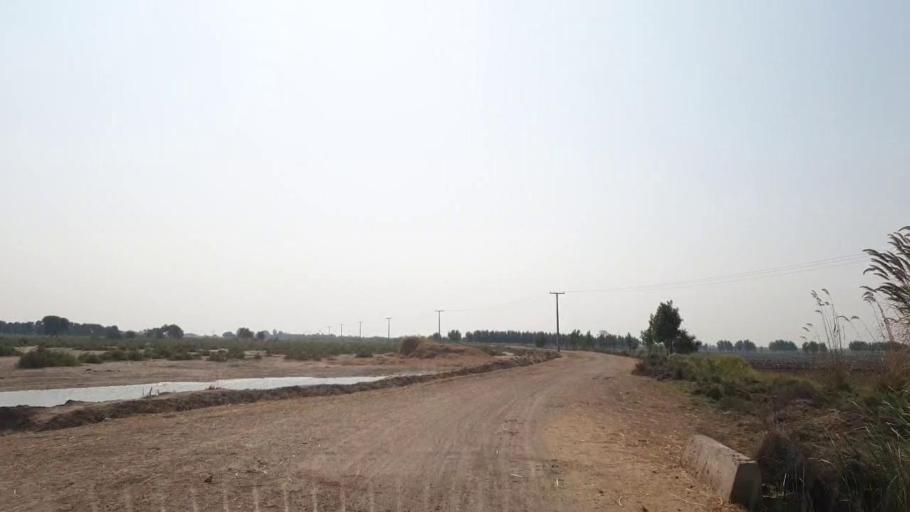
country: PK
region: Sindh
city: Tando Muhammad Khan
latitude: 25.0504
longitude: 68.4521
